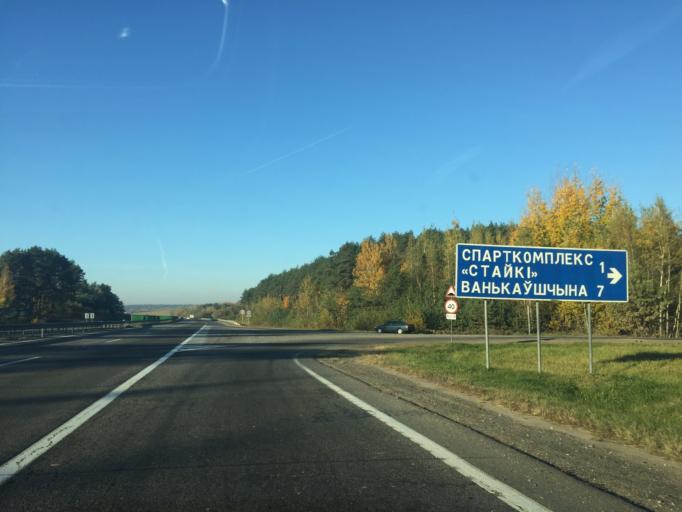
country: BY
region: Minsk
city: Pryvol'ny
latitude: 53.7941
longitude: 27.7411
